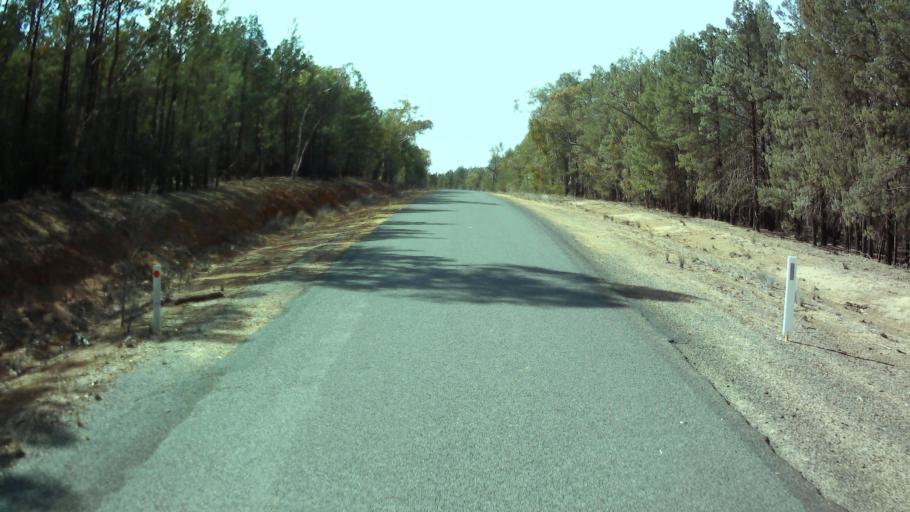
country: AU
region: New South Wales
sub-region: Weddin
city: Grenfell
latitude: -33.7348
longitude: 148.0400
